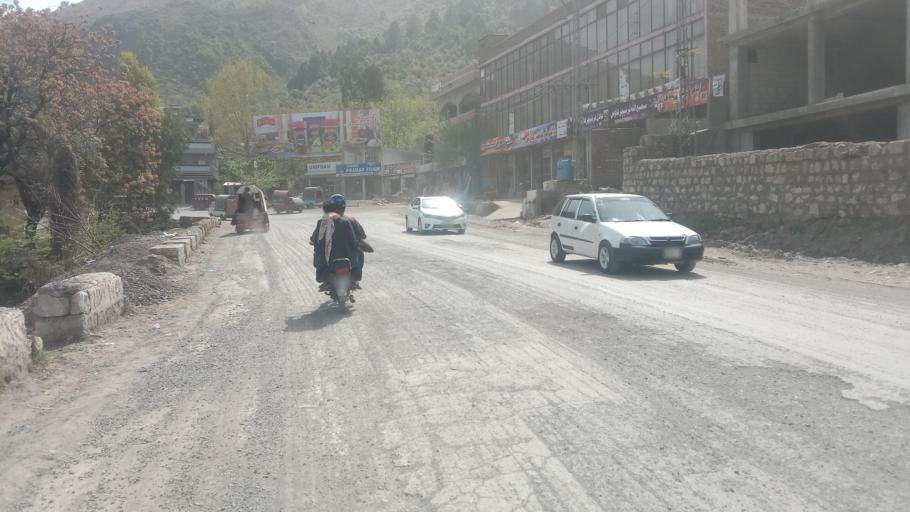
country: PK
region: Khyber Pakhtunkhwa
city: Abbottabad
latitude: 34.1263
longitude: 73.1926
